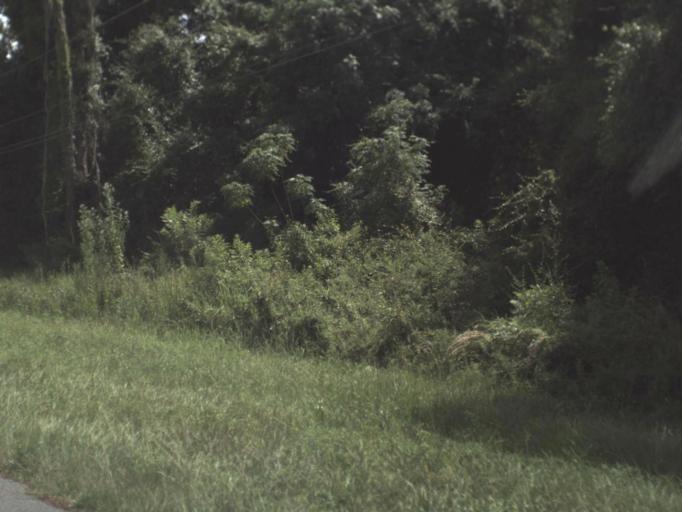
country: US
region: Florida
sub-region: Citrus County
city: Hernando
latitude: 28.9185
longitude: -82.3759
